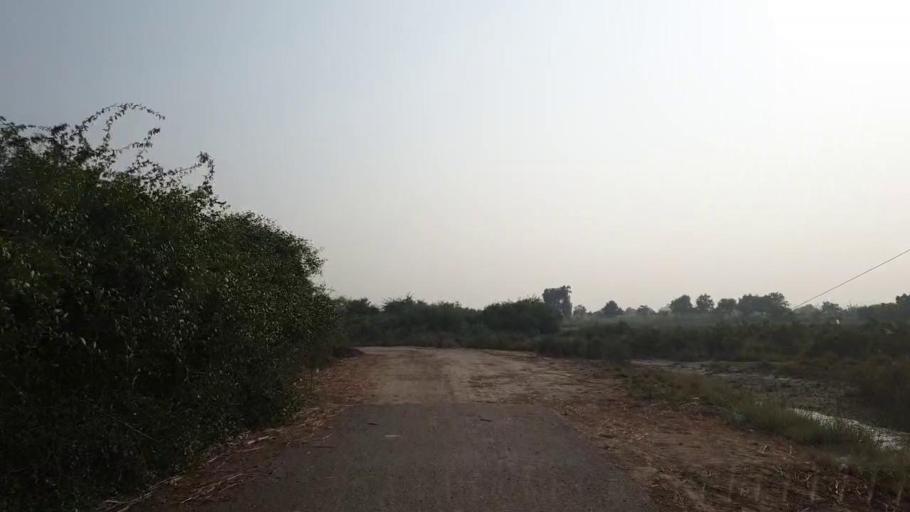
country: PK
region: Sindh
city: Tando Muhammad Khan
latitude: 25.1315
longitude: 68.6235
